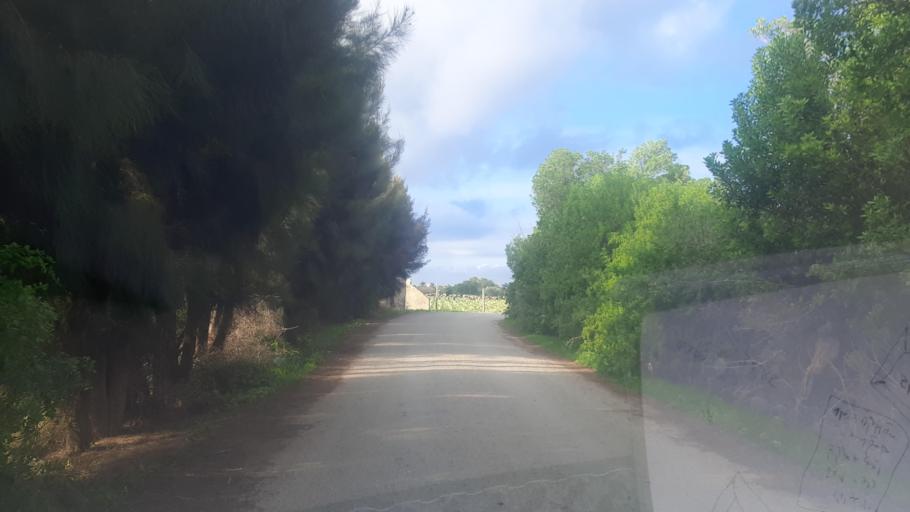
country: TN
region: Nabul
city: Manzil Bu Zalafah
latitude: 36.7095
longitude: 10.5013
